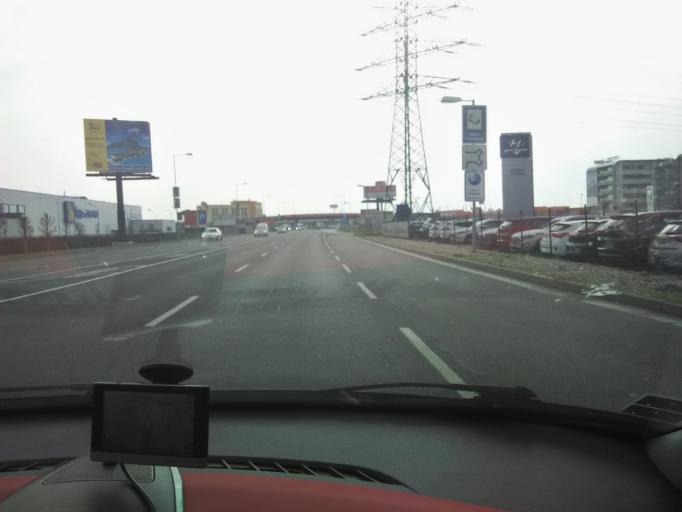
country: SK
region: Bratislavsky
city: Bratislava
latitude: 48.1653
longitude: 17.1788
